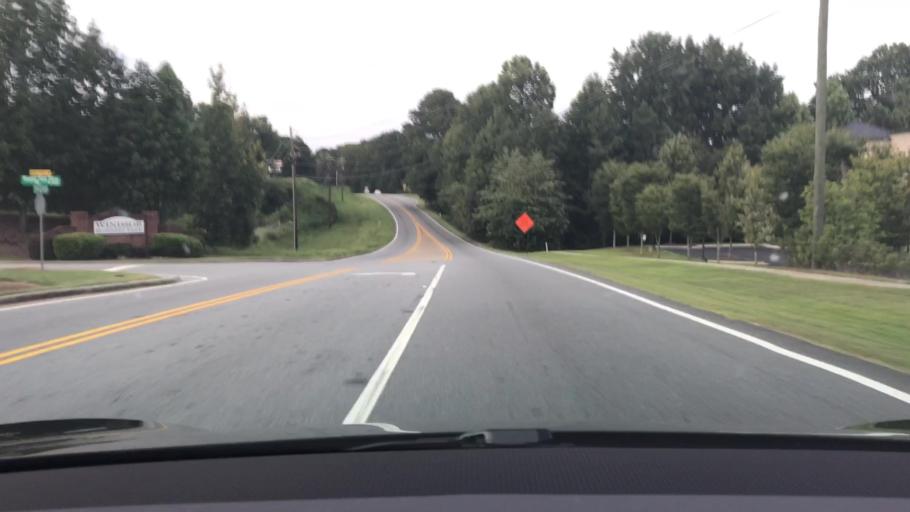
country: US
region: Georgia
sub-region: Gwinnett County
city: Suwanee
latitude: 34.0375
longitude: -84.0836
